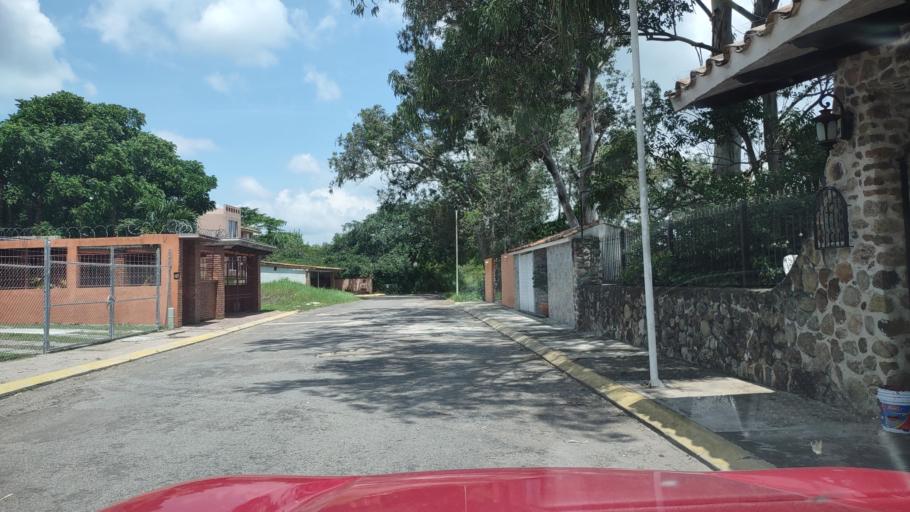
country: MX
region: Veracruz
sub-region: Emiliano Zapata
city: Dos Rios
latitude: 19.4648
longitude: -96.7906
